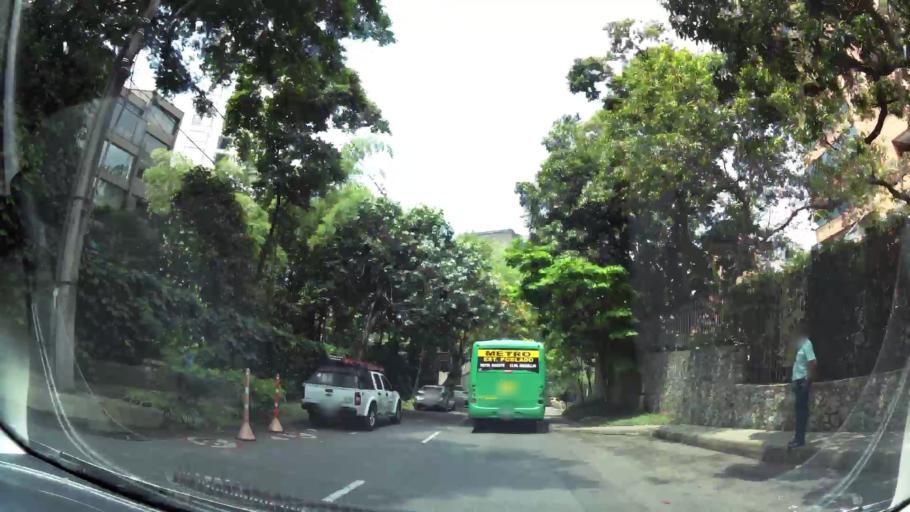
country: CO
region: Antioquia
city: Itagui
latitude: 6.2049
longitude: -75.5698
